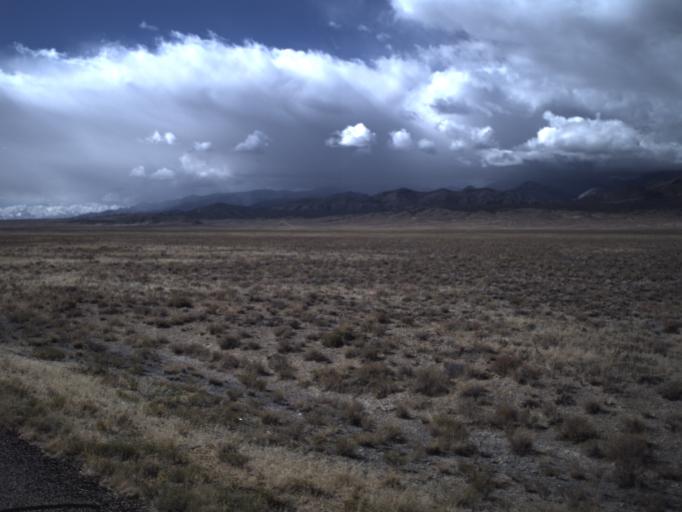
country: US
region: Nevada
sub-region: White Pine County
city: McGill
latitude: 38.9905
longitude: -114.0345
